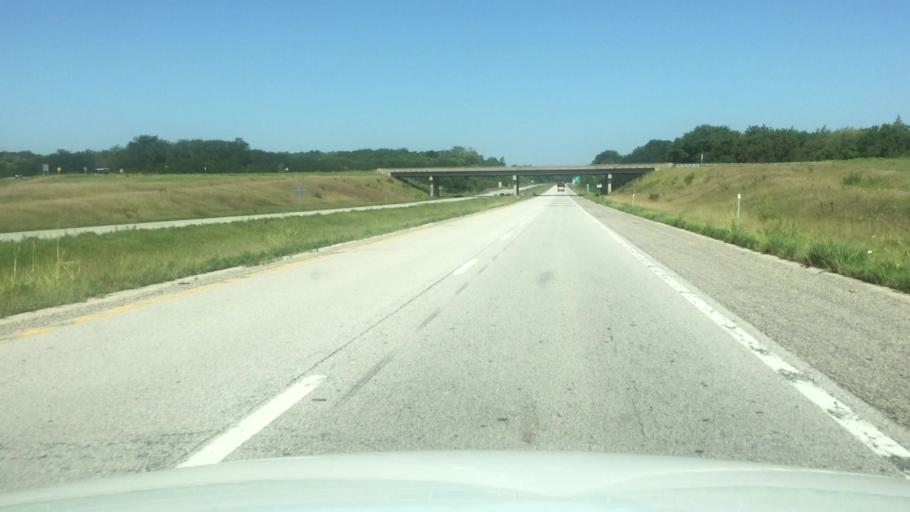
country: US
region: Missouri
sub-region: Buchanan County
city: Saint Joseph
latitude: 39.7161
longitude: -94.8179
